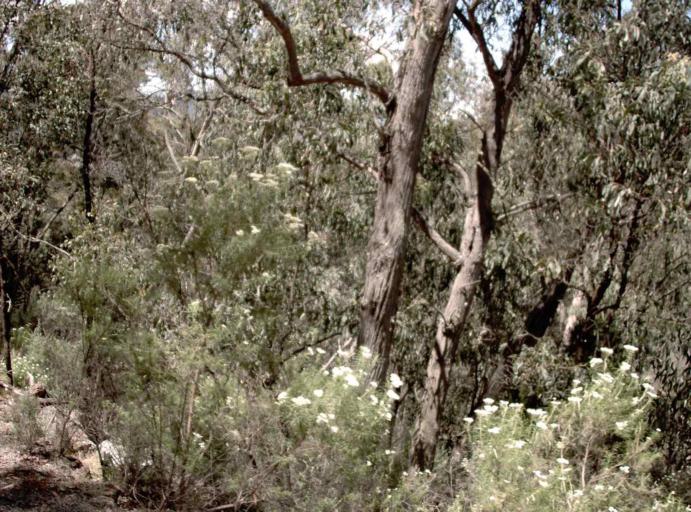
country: AU
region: New South Wales
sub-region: Snowy River
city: Jindabyne
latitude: -37.0828
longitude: 148.3343
